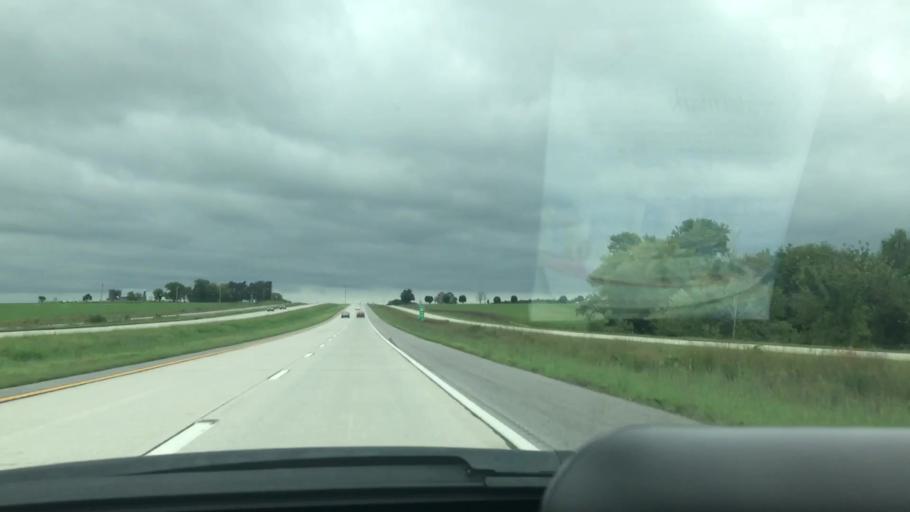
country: US
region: Missouri
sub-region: Greene County
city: Fair Grove
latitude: 37.4306
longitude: -93.1448
